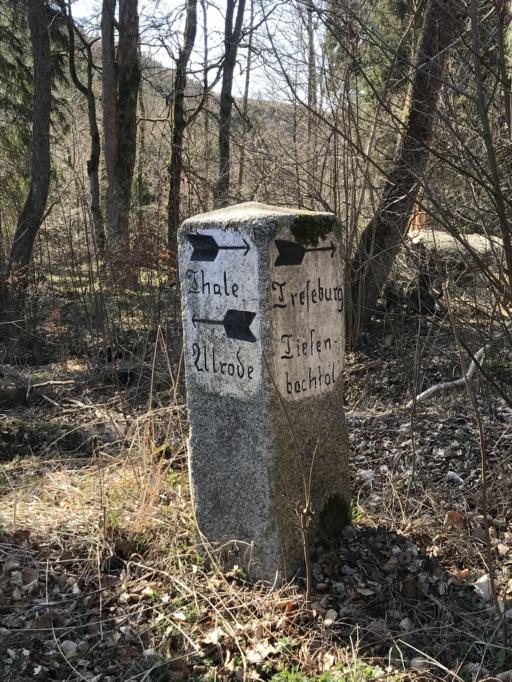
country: DE
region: Saxony-Anhalt
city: Friedrichsbrunn
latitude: 51.7008
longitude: 11.0076
